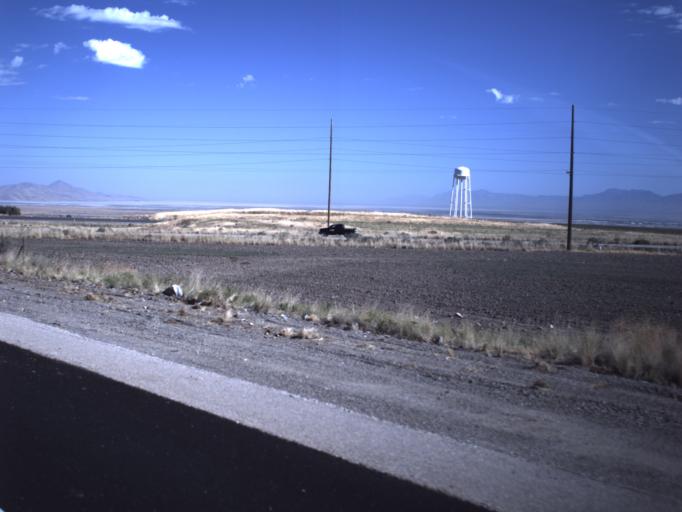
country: US
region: Utah
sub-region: Salt Lake County
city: Oquirrh
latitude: 40.6519
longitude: -112.0736
